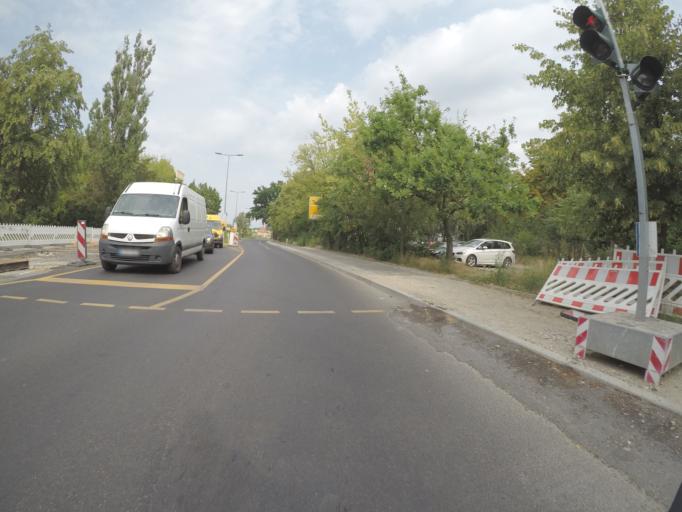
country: DE
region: Berlin
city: Buch
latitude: 52.6331
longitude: 13.5000
